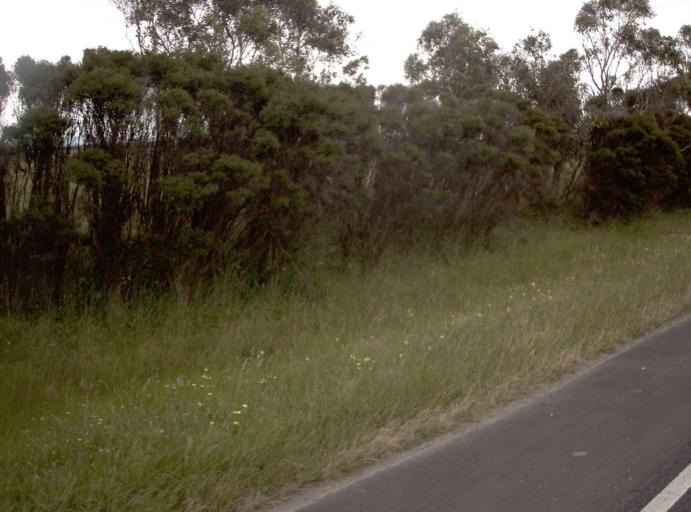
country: AU
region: Victoria
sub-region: Cardinia
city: Koo-Wee-Rup
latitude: -38.2130
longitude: 145.4492
